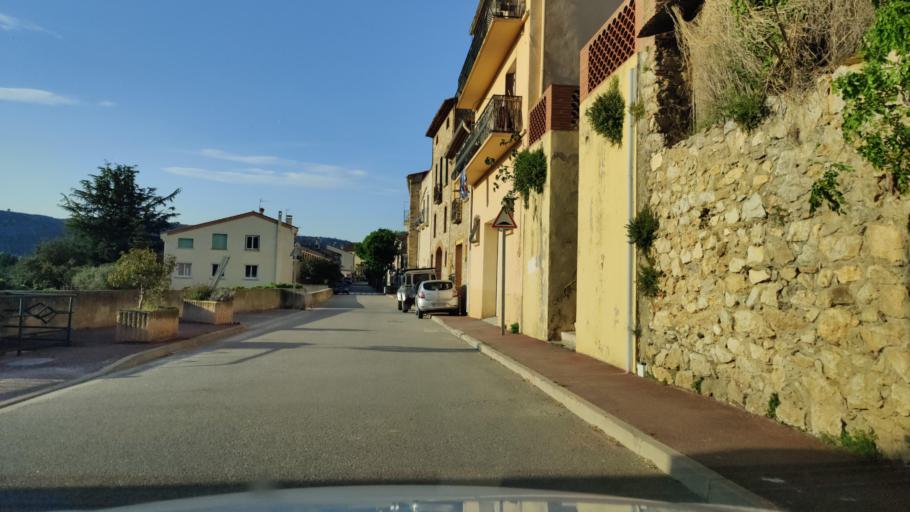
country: FR
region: Languedoc-Roussillon
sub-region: Departement des Pyrenees-Orientales
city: Estagel
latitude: 42.8116
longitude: 2.7444
